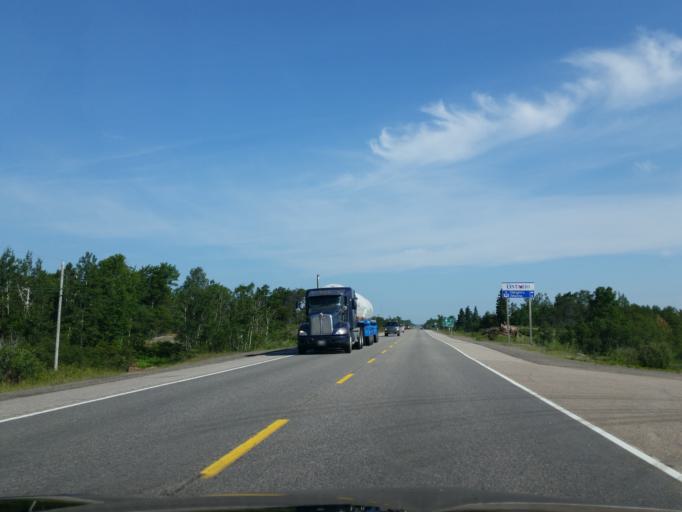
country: CA
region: Ontario
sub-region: Parry Sound District
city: Parry Sound
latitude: 45.7972
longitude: -80.5344
